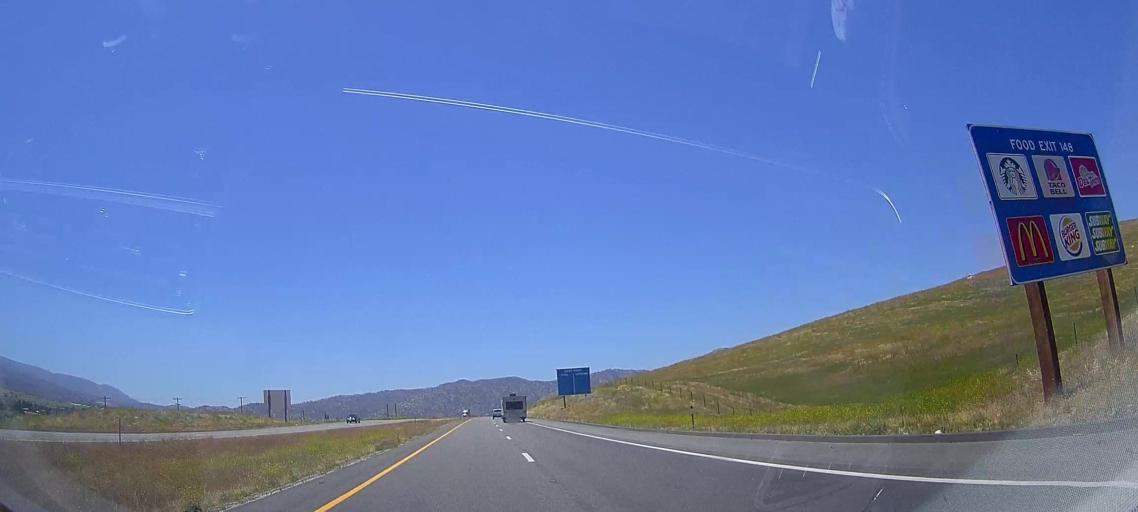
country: US
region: California
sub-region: Kern County
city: Tehachapi
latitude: 35.1398
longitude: -118.4578
